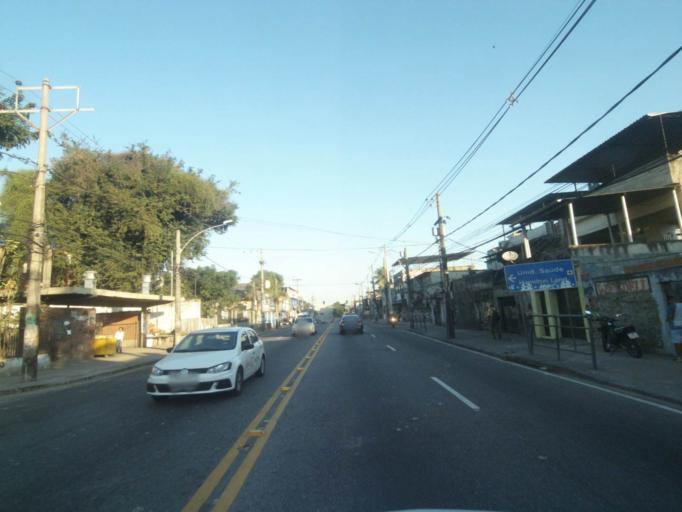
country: BR
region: Rio de Janeiro
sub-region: Sao Joao De Meriti
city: Sao Joao de Meriti
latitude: -22.9493
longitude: -43.3596
